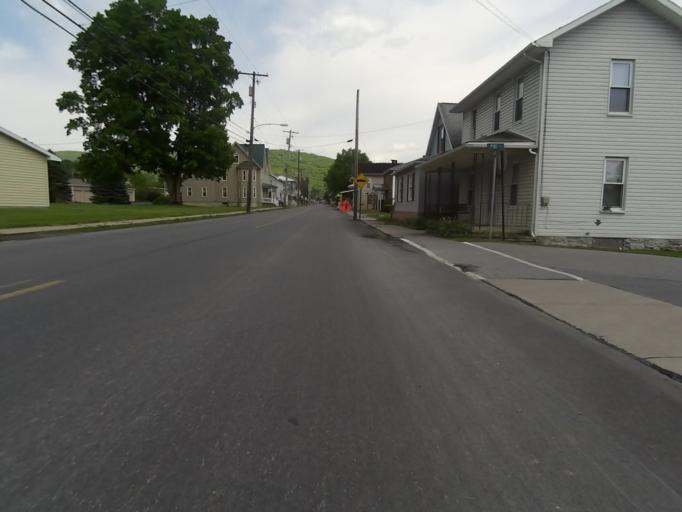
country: US
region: Pennsylvania
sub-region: Centre County
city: Zion
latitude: 41.0147
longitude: -77.6600
